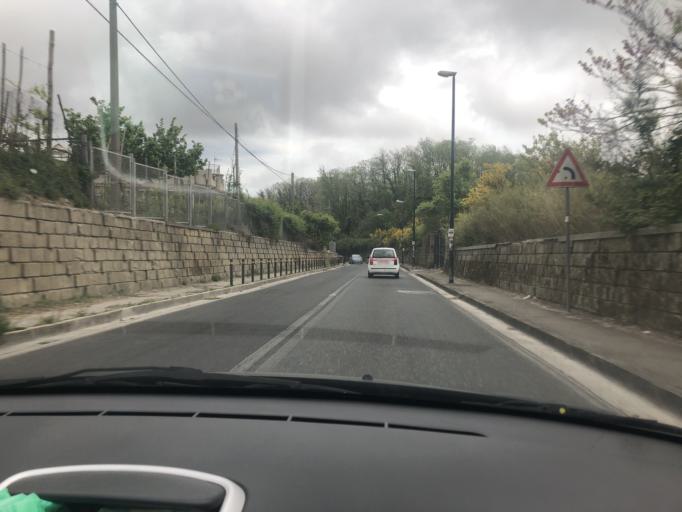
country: IT
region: Campania
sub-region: Provincia di Napoli
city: Torre Caracciolo
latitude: 40.8634
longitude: 14.1995
